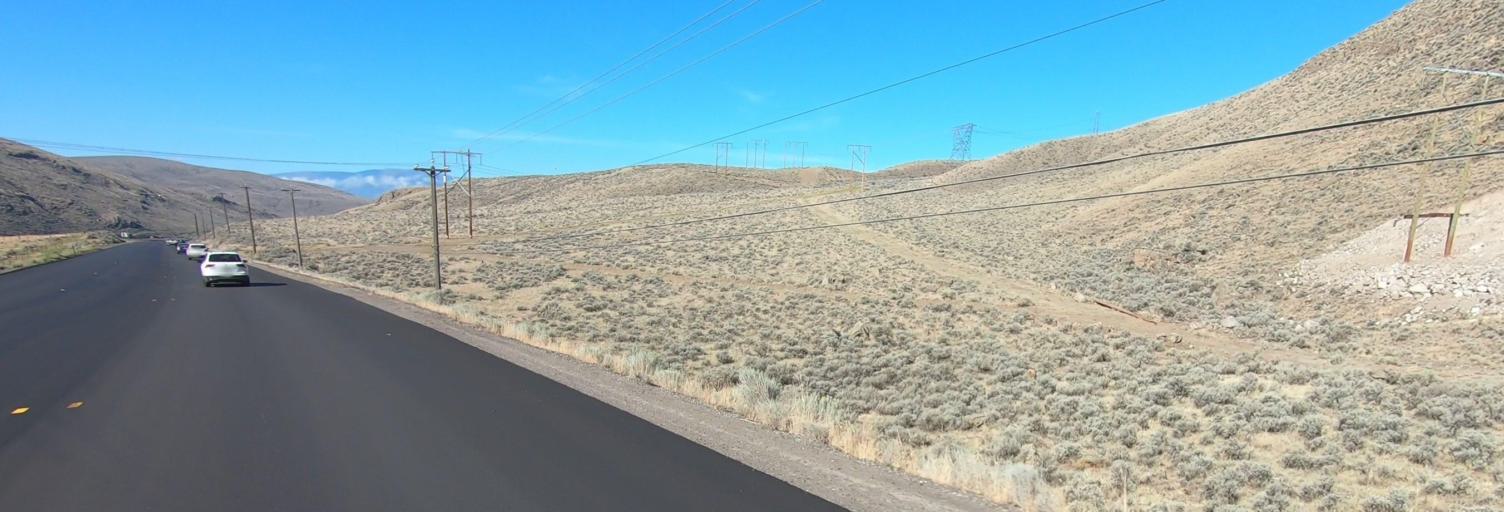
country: CA
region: British Columbia
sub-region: Thompson-Nicola Regional District
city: Ashcroft
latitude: 50.7899
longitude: -121.1767
